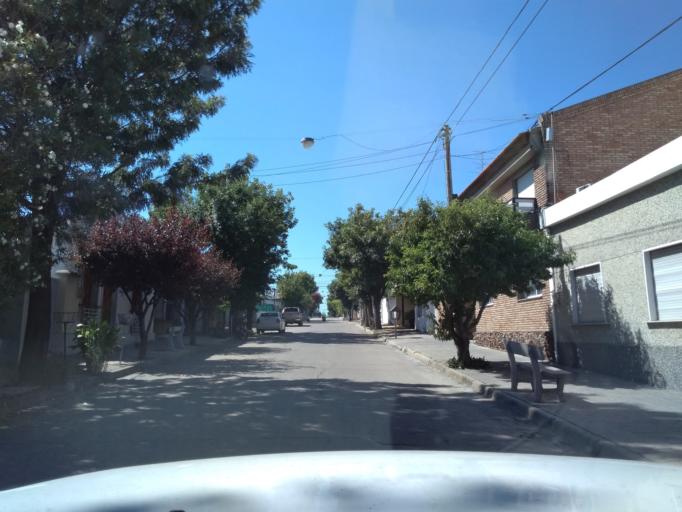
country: UY
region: Florida
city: Florida
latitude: -34.1007
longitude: -56.2191
